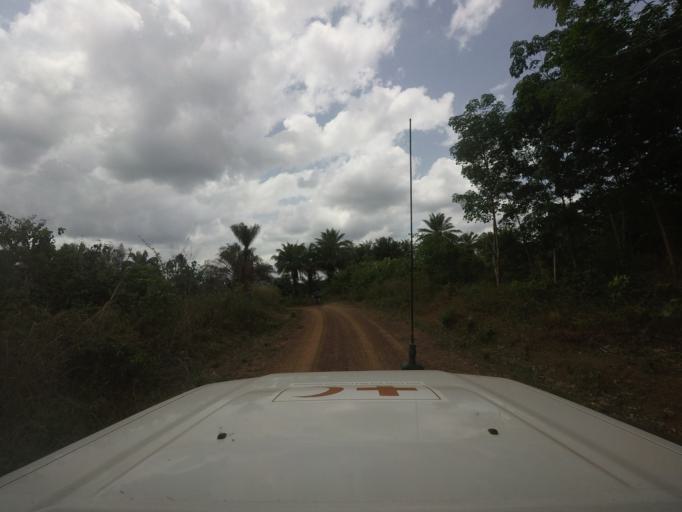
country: GN
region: Nzerekore
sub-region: Yomou
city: Yomou
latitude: 7.2657
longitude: -9.1875
